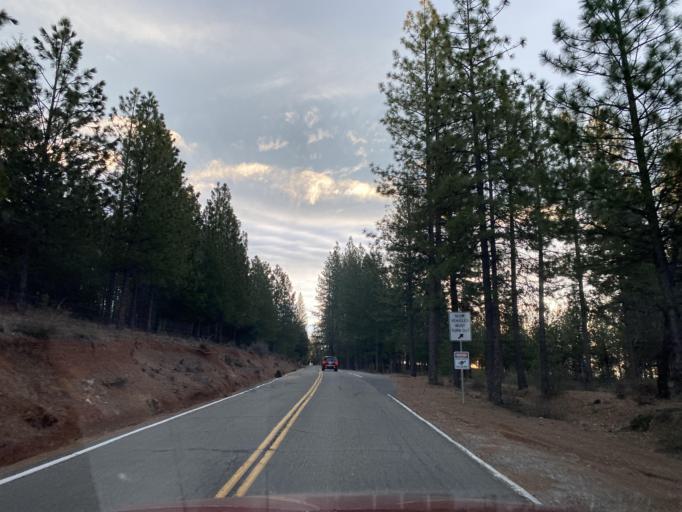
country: US
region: California
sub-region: Amador County
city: Pine Grove
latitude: 38.5010
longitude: -120.6448
